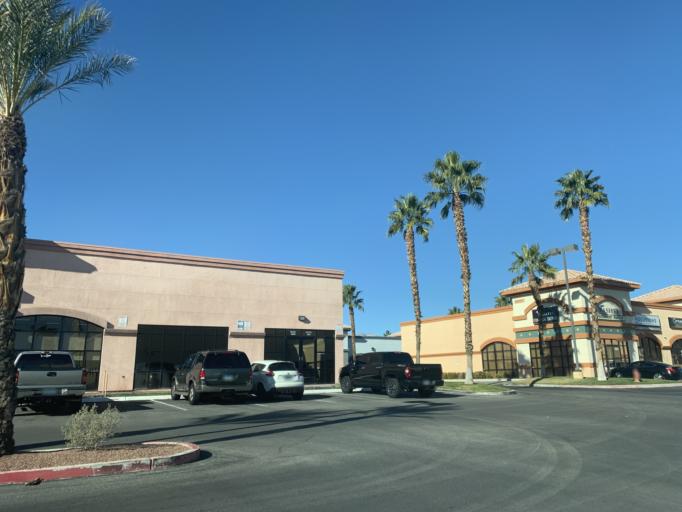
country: US
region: Nevada
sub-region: Clark County
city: Spring Valley
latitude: 36.1262
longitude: -115.2800
